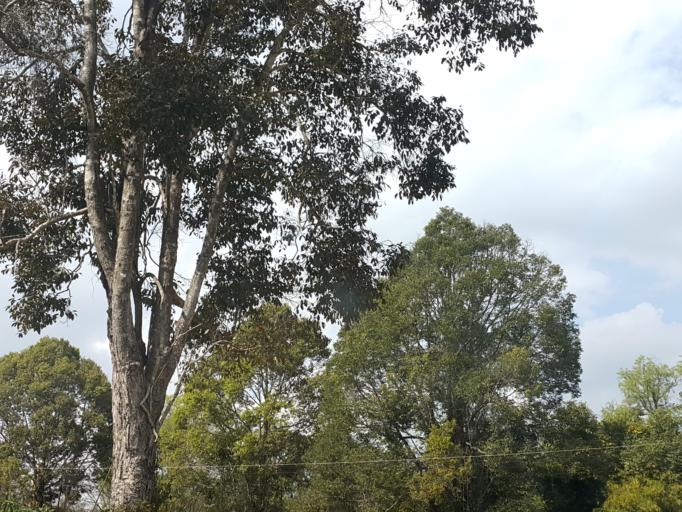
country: TH
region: Chiang Mai
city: Om Koi
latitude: 17.8011
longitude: 98.3666
